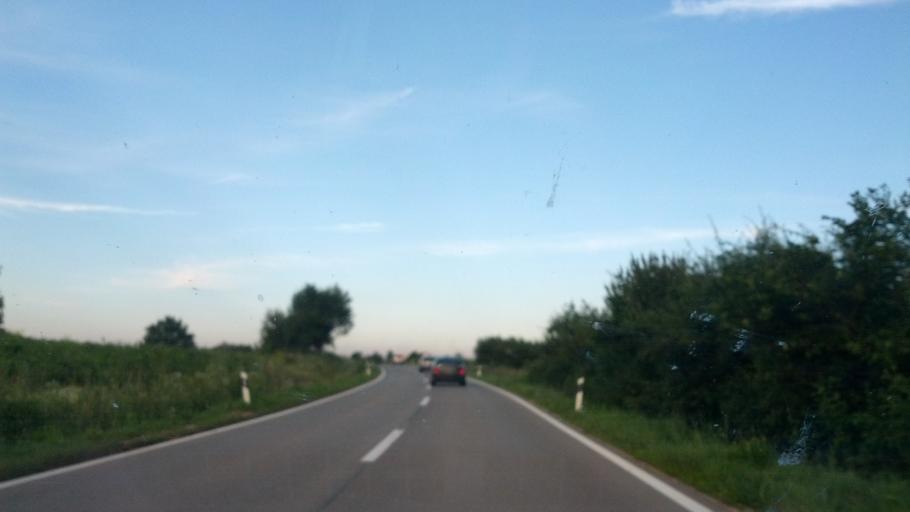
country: BA
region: Federation of Bosnia and Herzegovina
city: Izacic
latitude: 44.8789
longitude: 15.7383
